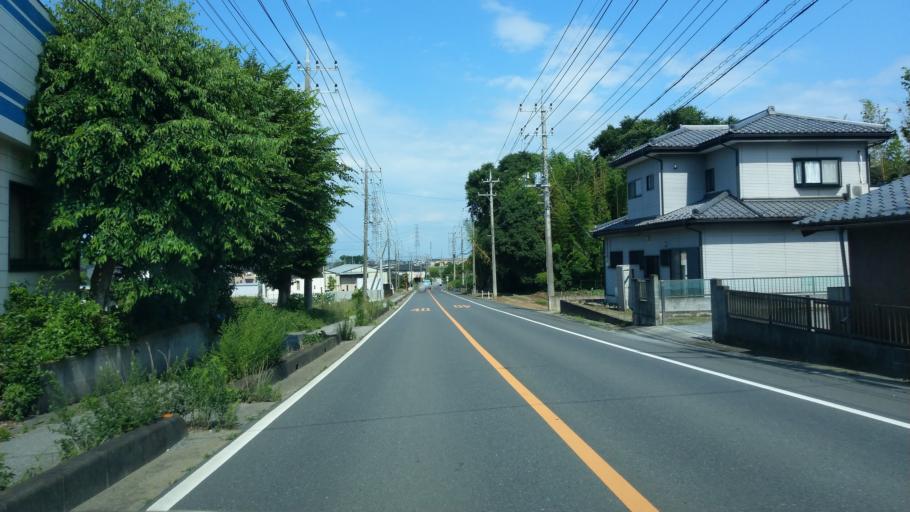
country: JP
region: Saitama
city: Kodamacho-kodamaminami
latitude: 36.2047
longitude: 139.1560
